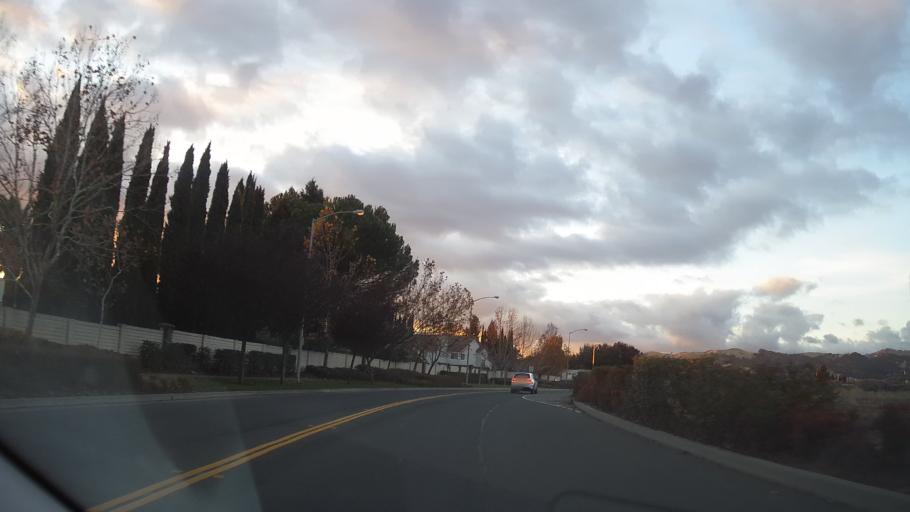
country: US
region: California
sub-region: Solano County
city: Fairfield
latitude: 38.2873
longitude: -122.0080
